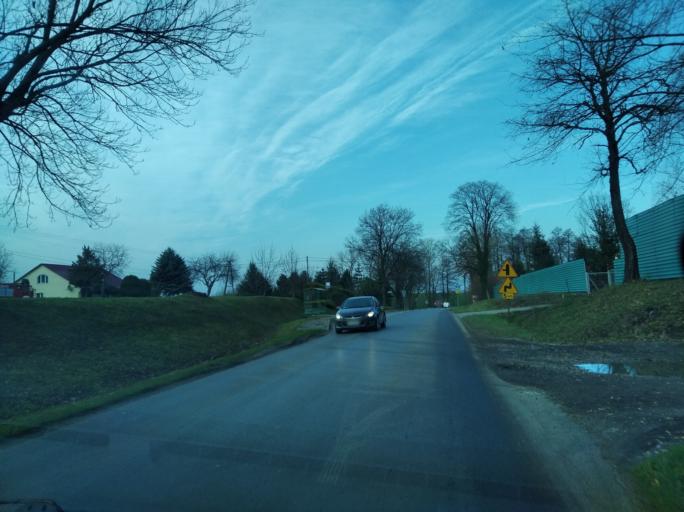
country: PL
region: Subcarpathian Voivodeship
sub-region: Powiat ropczycko-sedziszowski
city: Iwierzyce
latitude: 50.0477
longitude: 21.7448
